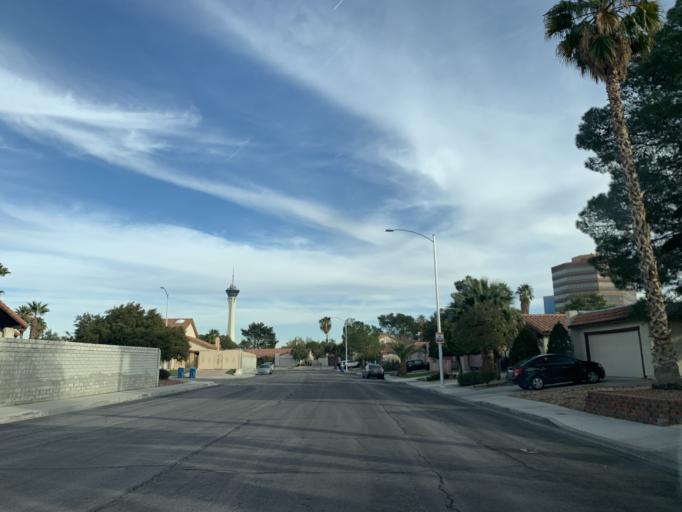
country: US
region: Nevada
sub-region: Clark County
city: Las Vegas
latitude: 36.1465
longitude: -115.1763
